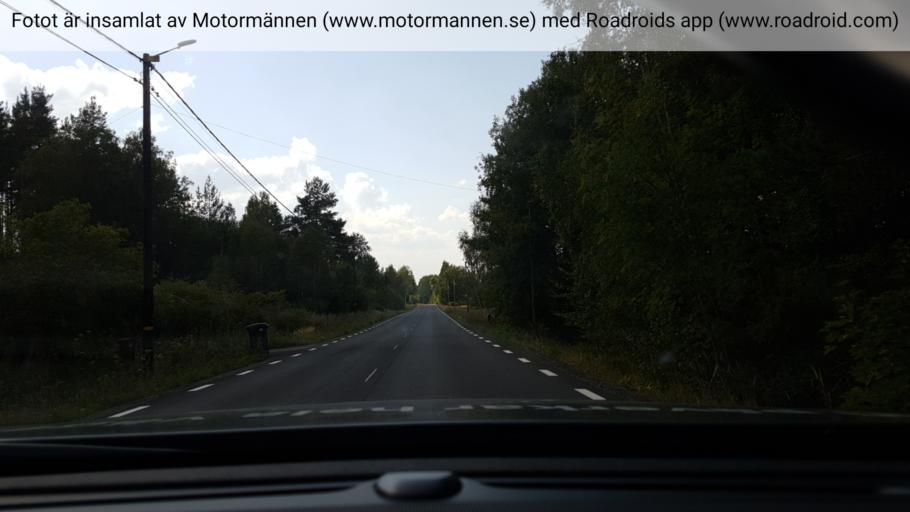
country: SE
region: Dalarna
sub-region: Faluns Kommun
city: Svardsjo
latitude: 60.7438
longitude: 15.9427
